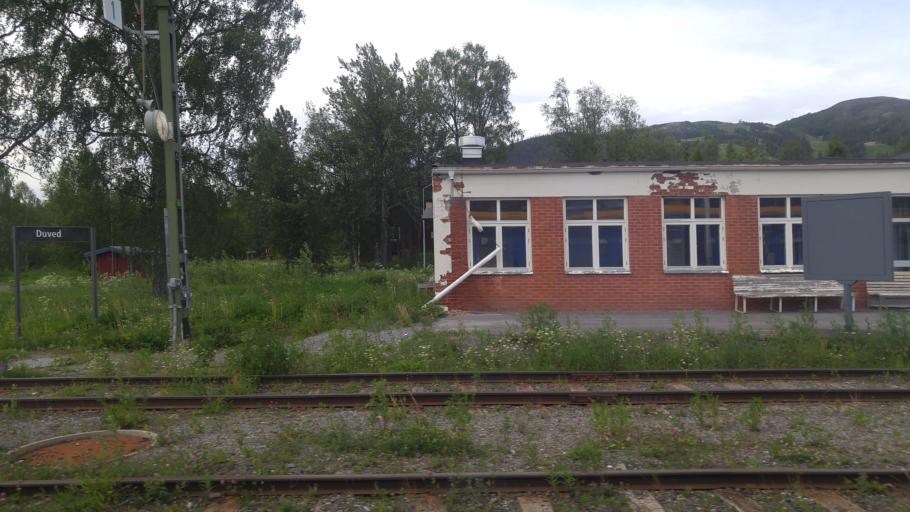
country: SE
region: Jaemtland
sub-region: Are Kommun
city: Are
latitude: 63.3898
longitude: 12.9171
